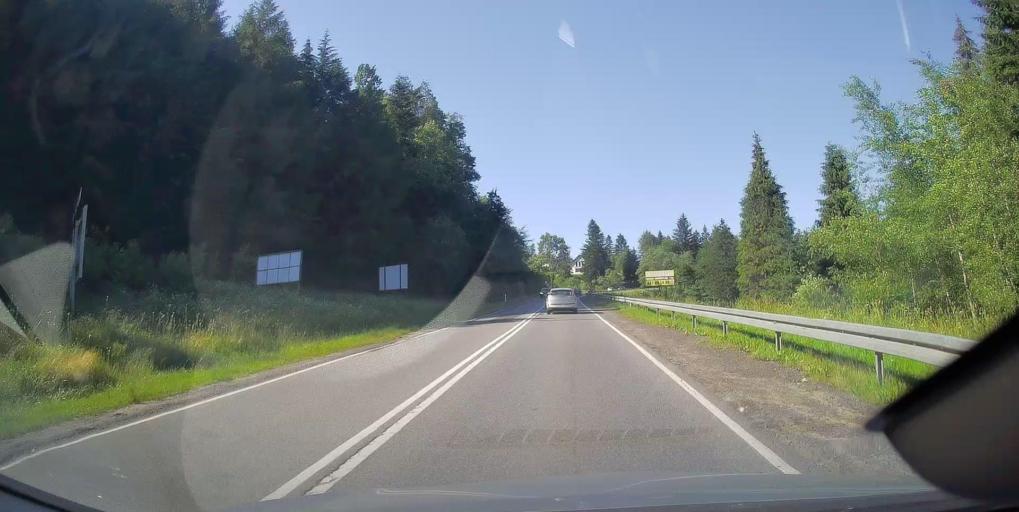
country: PL
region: Lesser Poland Voivodeship
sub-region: Powiat nowosadecki
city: Krynica-Zdroj
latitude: 49.4457
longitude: 20.9503
